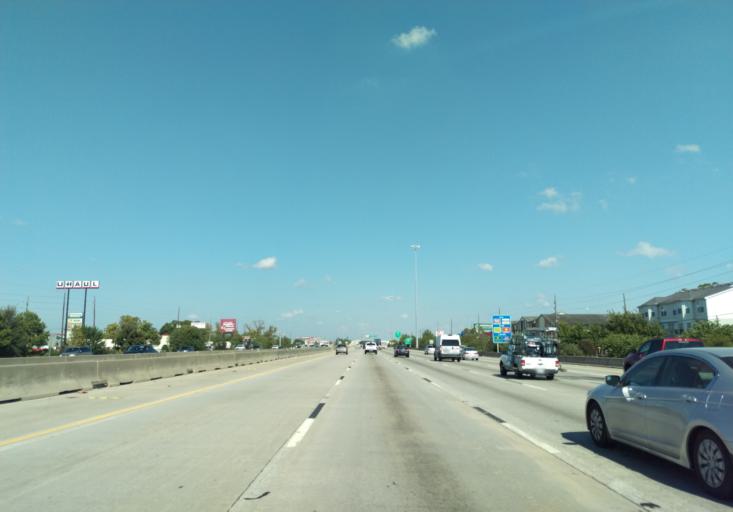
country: US
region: Texas
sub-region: Harris County
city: Spring
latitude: 30.0035
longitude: -95.4265
